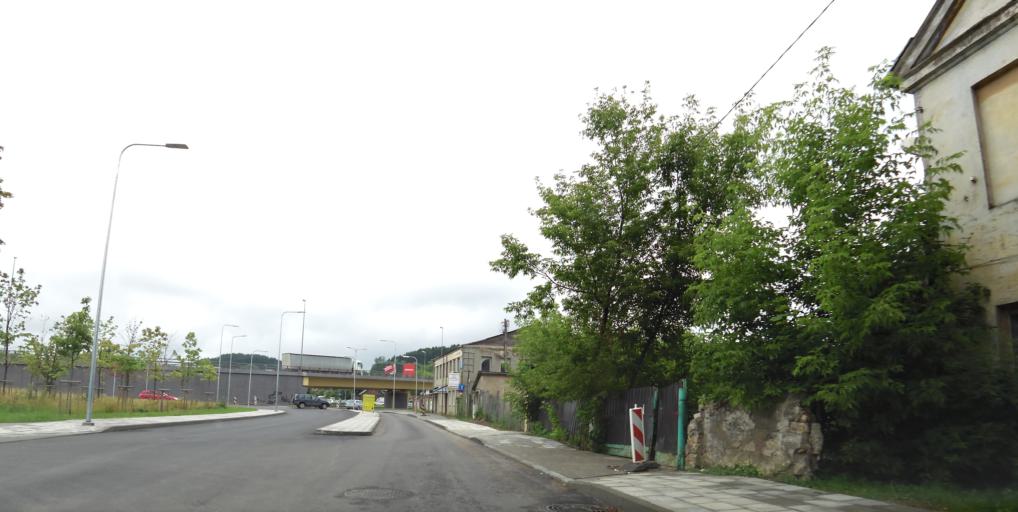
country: LT
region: Vilnius County
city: Seskine
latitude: 54.7011
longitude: 25.2657
